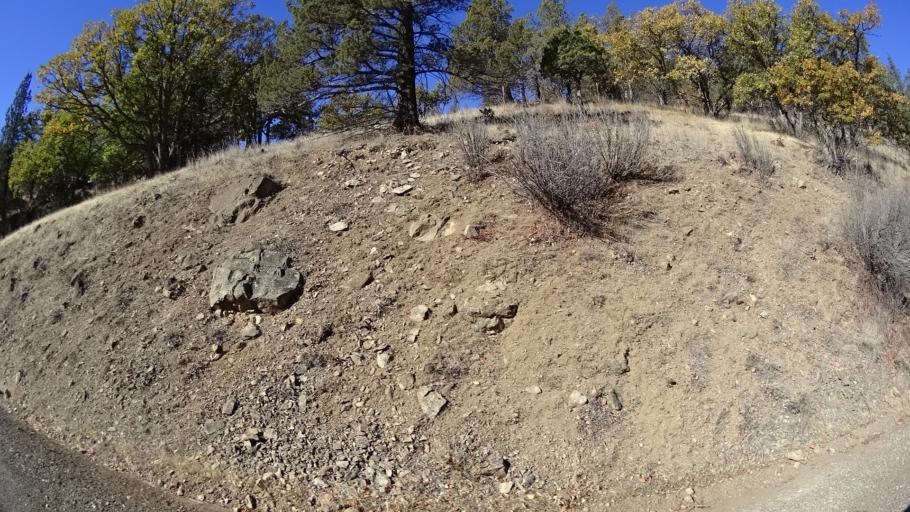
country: US
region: California
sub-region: Siskiyou County
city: Montague
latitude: 41.9325
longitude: -122.3547
